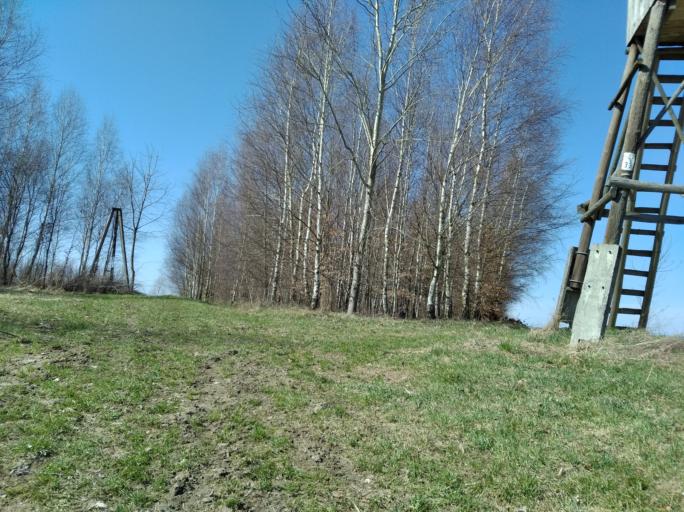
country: PL
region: Subcarpathian Voivodeship
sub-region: Powiat strzyzowski
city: Strzyzow
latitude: 49.8529
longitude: 21.8253
